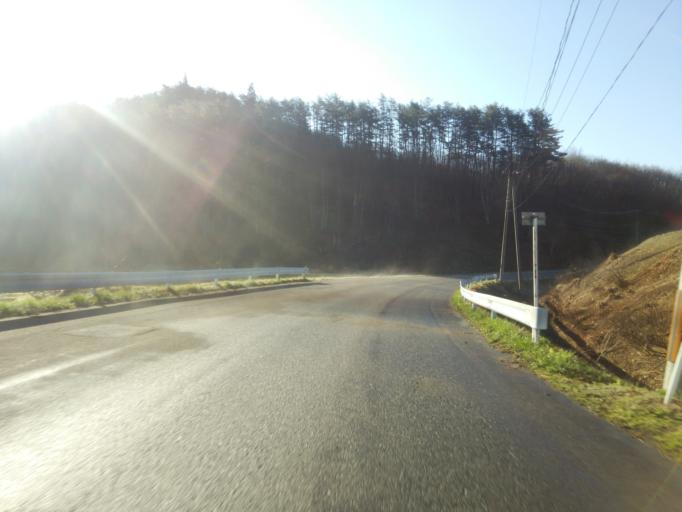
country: JP
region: Fukushima
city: Kitakata
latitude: 37.7041
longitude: 139.7857
